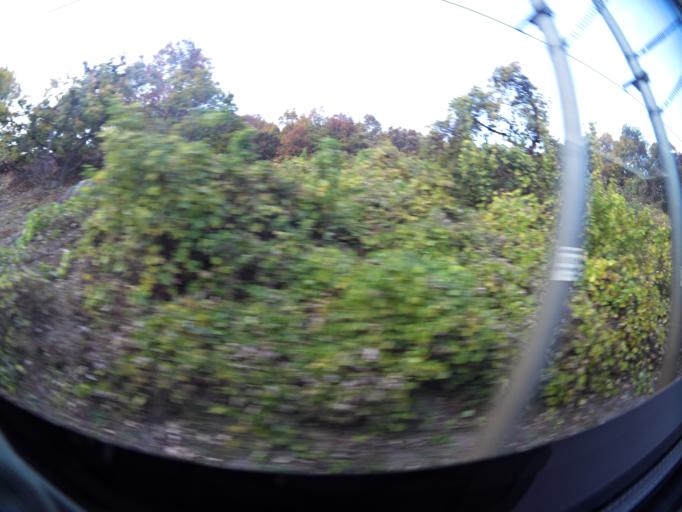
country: KR
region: Gyeongsangbuk-do
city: Gimcheon
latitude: 36.1688
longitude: 128.0056
